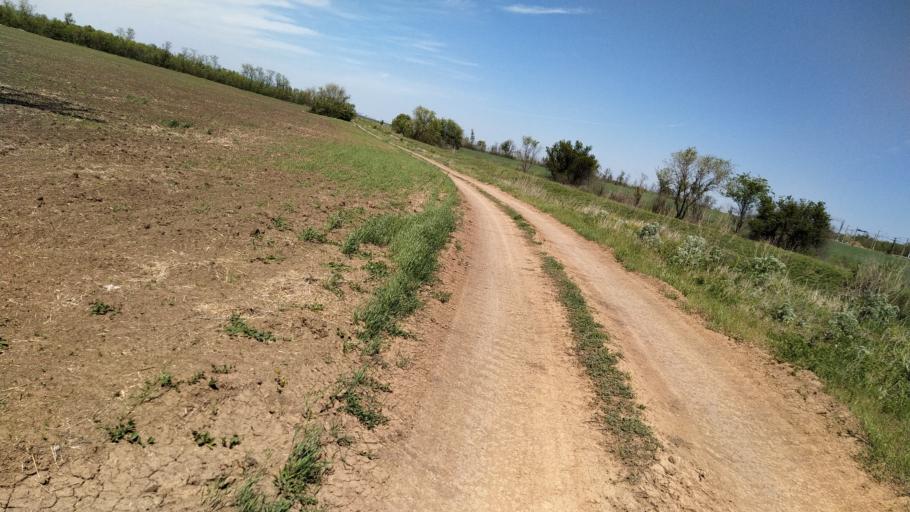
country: RU
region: Rostov
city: Kuleshovka
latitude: 47.0405
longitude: 39.6436
